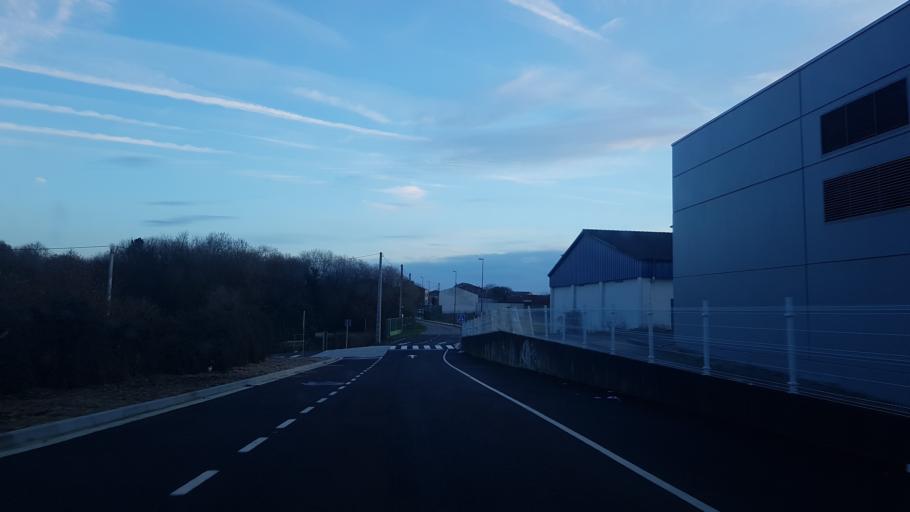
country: ES
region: Galicia
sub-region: Provincia de Lugo
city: Lugo
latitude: 43.0380
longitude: -7.5650
